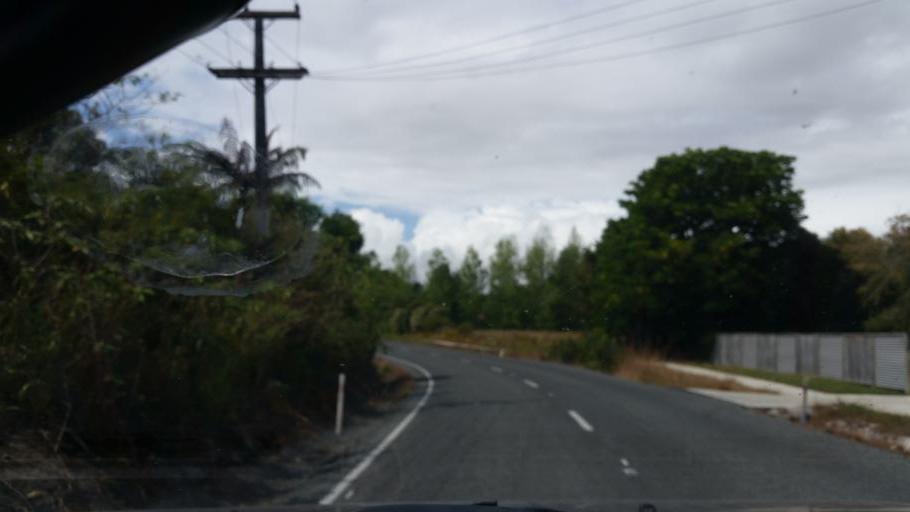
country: NZ
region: Auckland
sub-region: Auckland
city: Wellsford
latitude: -36.1274
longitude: 174.5613
